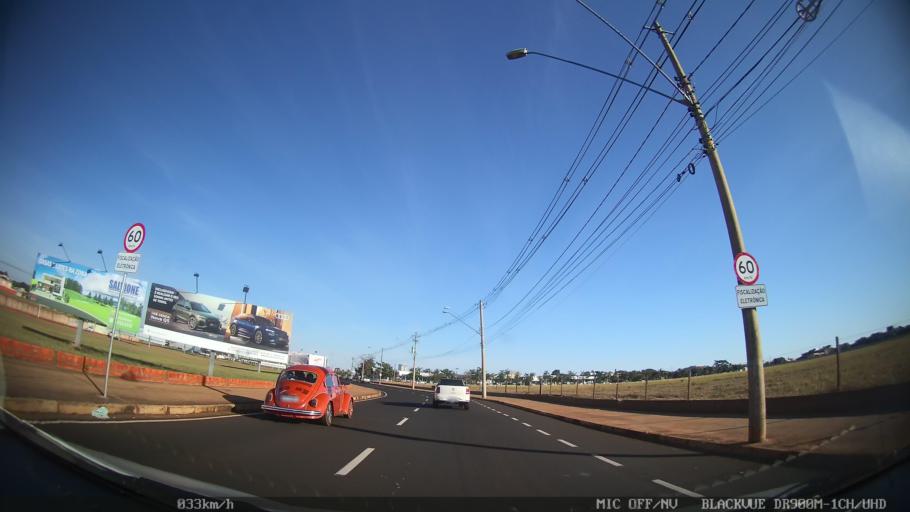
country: BR
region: Sao Paulo
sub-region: Sao Jose Do Rio Preto
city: Sao Jose do Rio Preto
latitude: -20.8519
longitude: -49.4134
